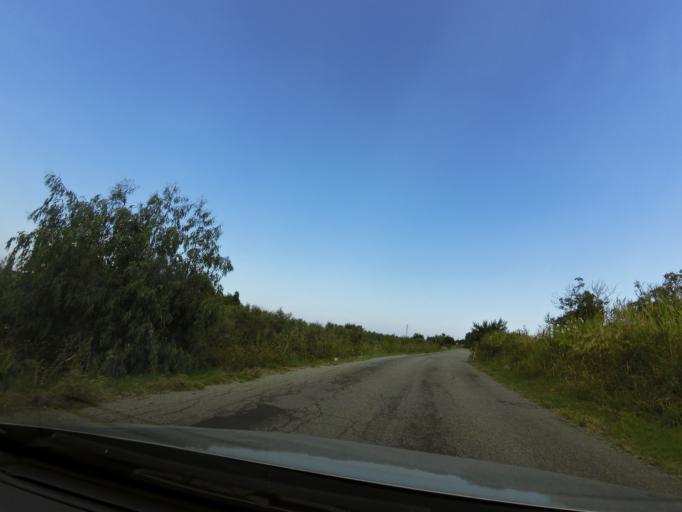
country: IT
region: Calabria
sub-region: Provincia di Reggio Calabria
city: Monasterace Marina
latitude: 38.4222
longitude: 16.5519
